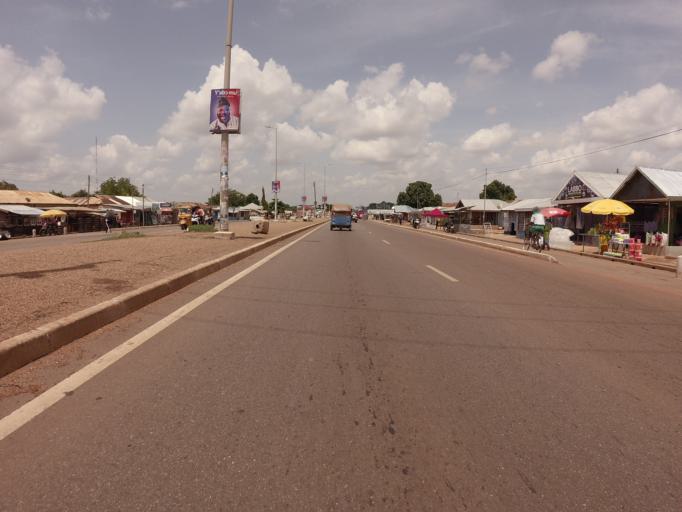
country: GH
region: Northern
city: Tamale
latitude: 9.3989
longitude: -0.8311
